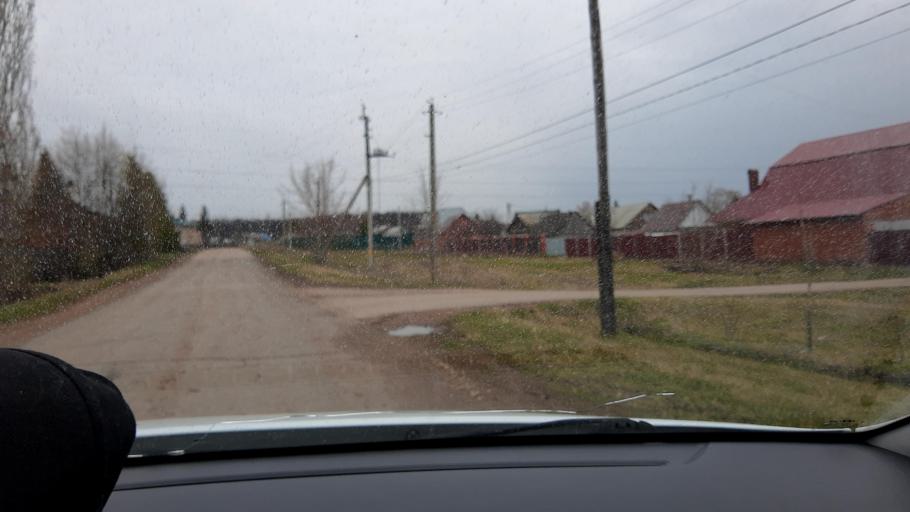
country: RU
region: Bashkortostan
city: Avdon
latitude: 54.6203
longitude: 55.6399
